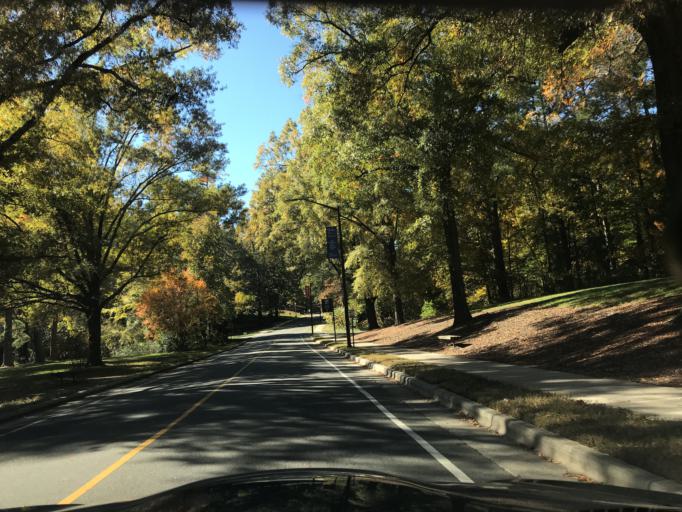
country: US
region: North Carolina
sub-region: Durham County
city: Durham
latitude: 36.0003
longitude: -78.9264
